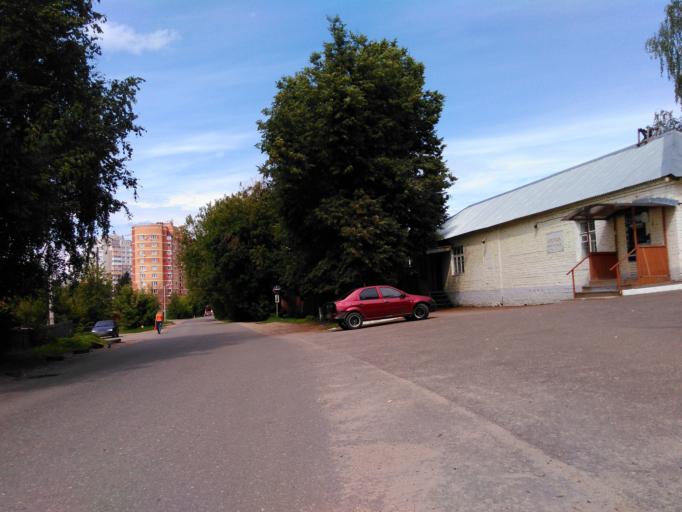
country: RU
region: Moskovskaya
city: Pravdinskiy
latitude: 56.0593
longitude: 37.8510
